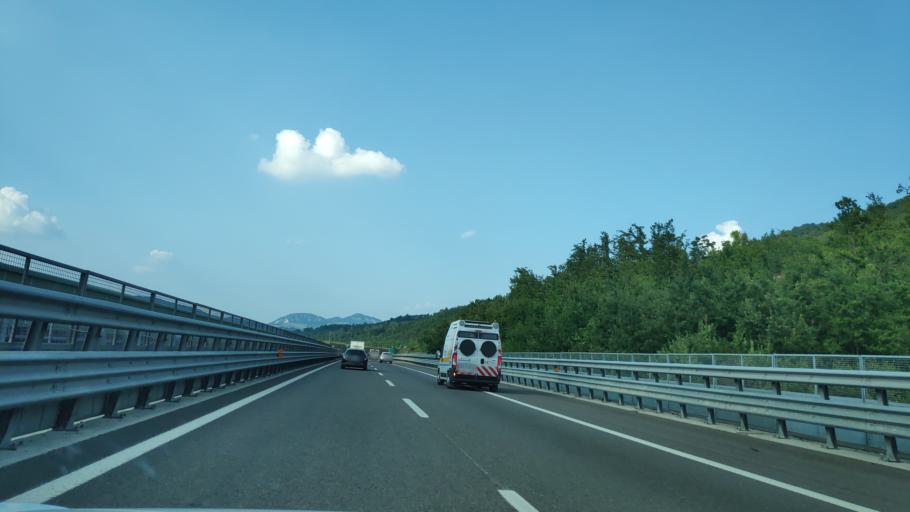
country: IT
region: Emilia-Romagna
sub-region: Provincia di Bologna
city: Grizzana
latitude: 44.2347
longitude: 11.1849
